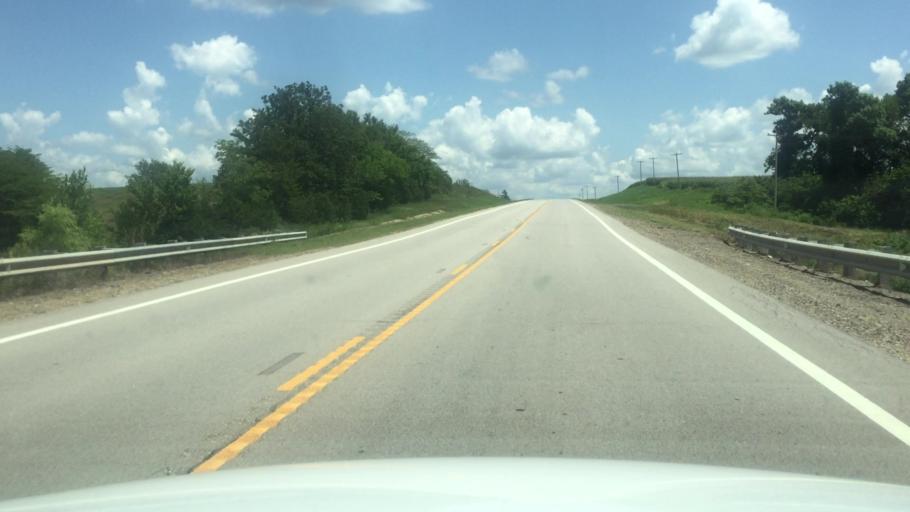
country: US
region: Kansas
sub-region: Brown County
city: Horton
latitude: 39.6672
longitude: -95.4722
